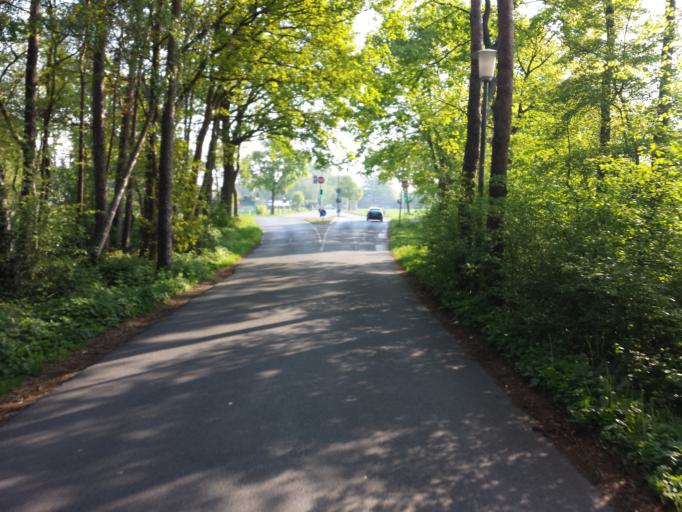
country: DE
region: North Rhine-Westphalia
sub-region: Regierungsbezirk Detmold
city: Guetersloh
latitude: 51.9284
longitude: 8.3588
